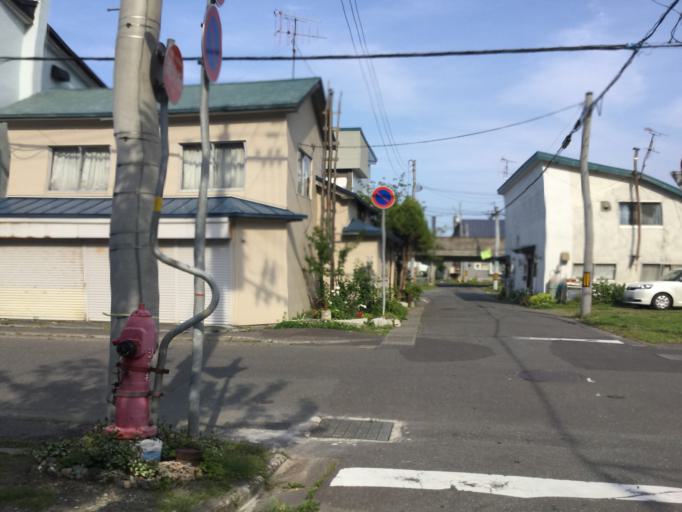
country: JP
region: Hokkaido
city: Wakkanai
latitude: 45.4079
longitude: 141.6742
